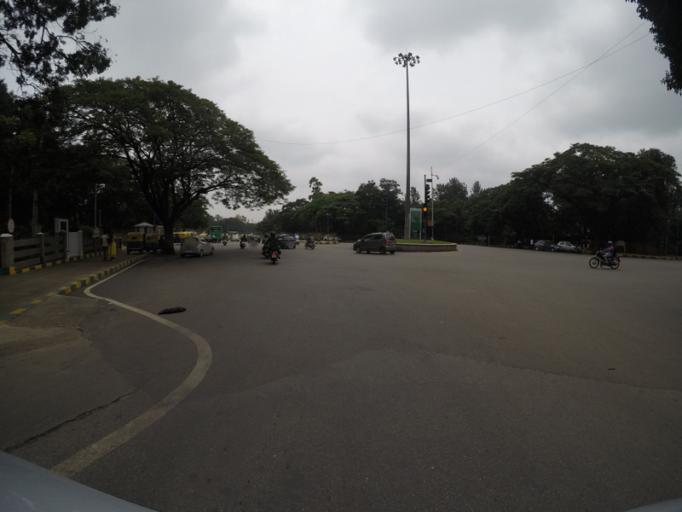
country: IN
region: Karnataka
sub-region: Bangalore Urban
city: Yelahanka
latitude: 13.0458
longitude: 77.5566
